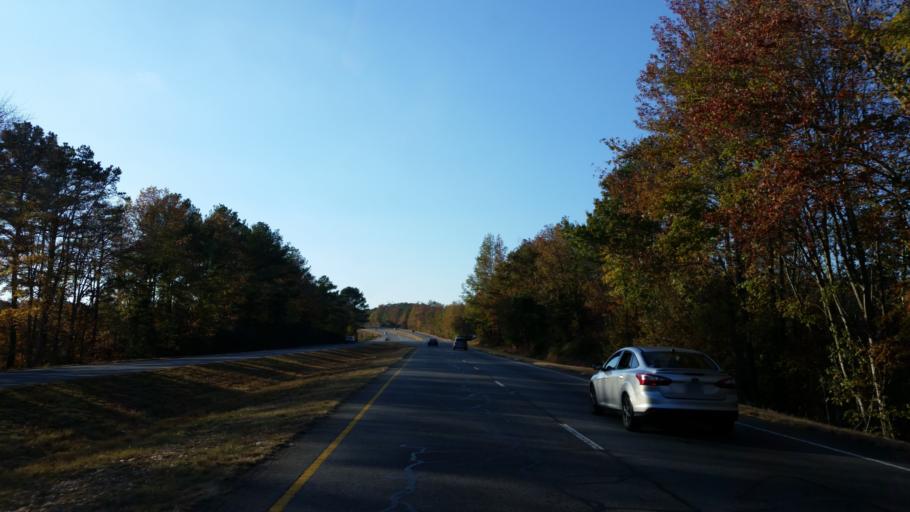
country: US
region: Georgia
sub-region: Bartow County
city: Euharlee
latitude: 34.2211
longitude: -84.8804
